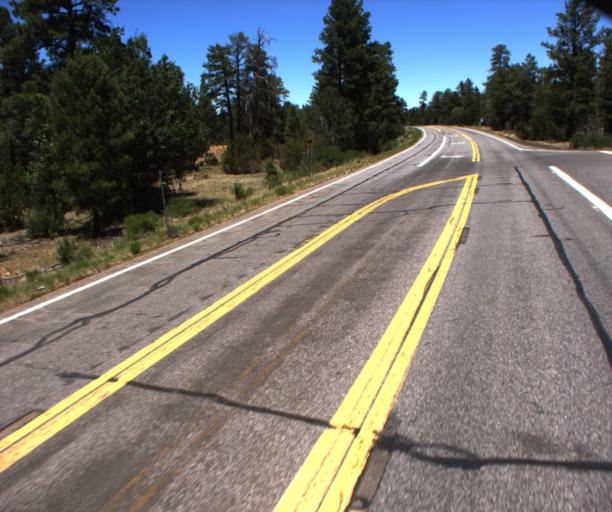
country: US
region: Arizona
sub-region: Gila County
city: Star Valley
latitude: 34.6676
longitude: -111.1075
